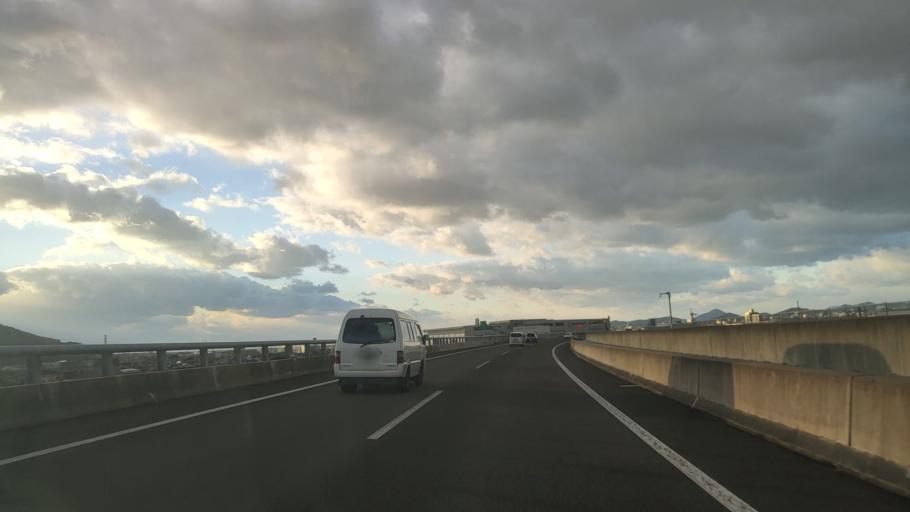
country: JP
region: Ehime
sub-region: Shikoku-chuo Shi
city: Matsuyama
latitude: 33.7888
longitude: 132.8079
